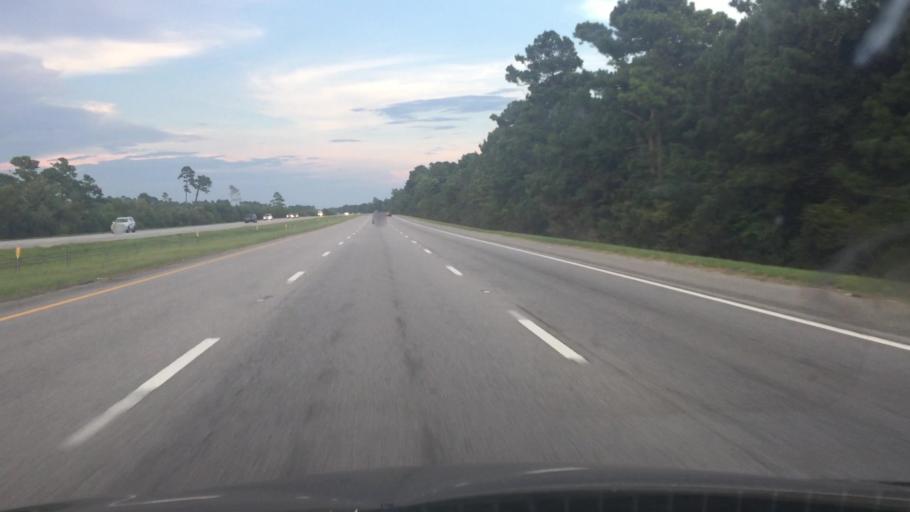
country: US
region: South Carolina
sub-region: Horry County
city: Myrtle Beach
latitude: 33.7664
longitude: -78.8316
